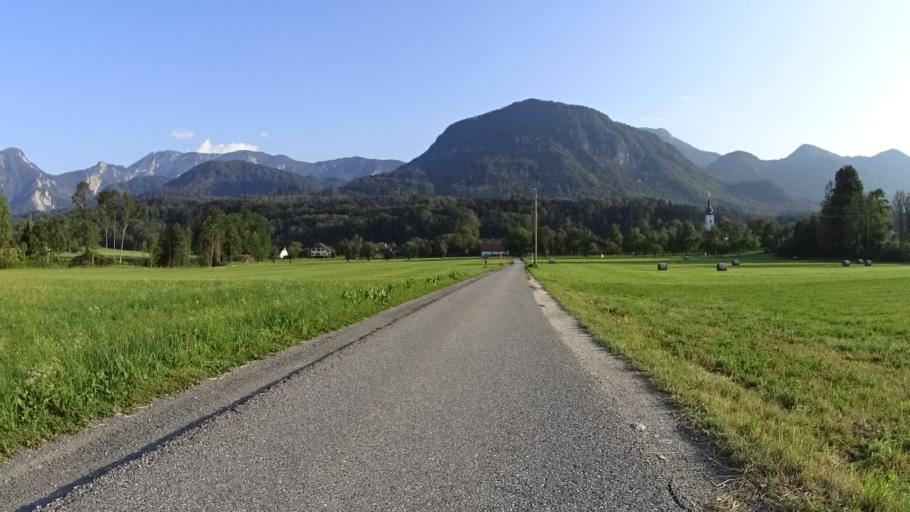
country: AT
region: Carinthia
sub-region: Politischer Bezirk Villach Land
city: Sankt Jakob
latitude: 46.5333
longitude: 14.0879
